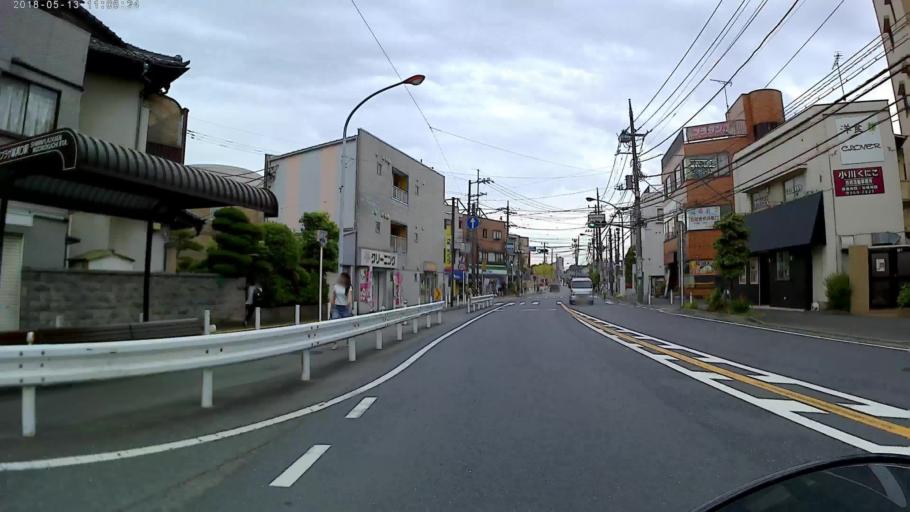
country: JP
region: Tokyo
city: Chofugaoka
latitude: 35.5966
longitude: 139.6129
